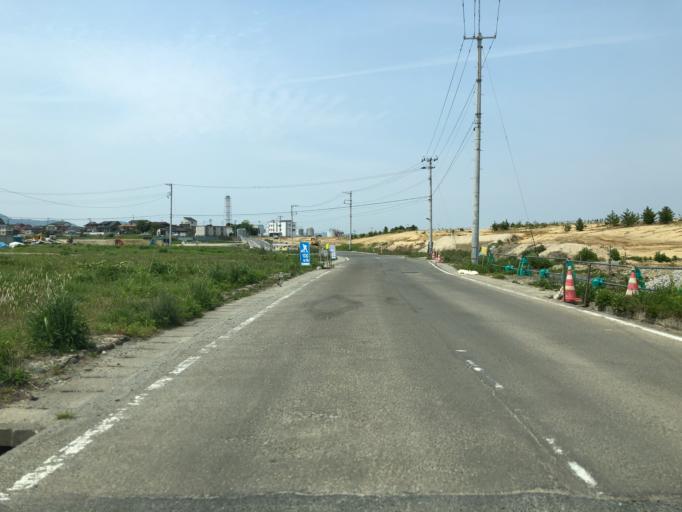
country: JP
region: Miyagi
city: Marumori
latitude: 37.8261
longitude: 140.9665
